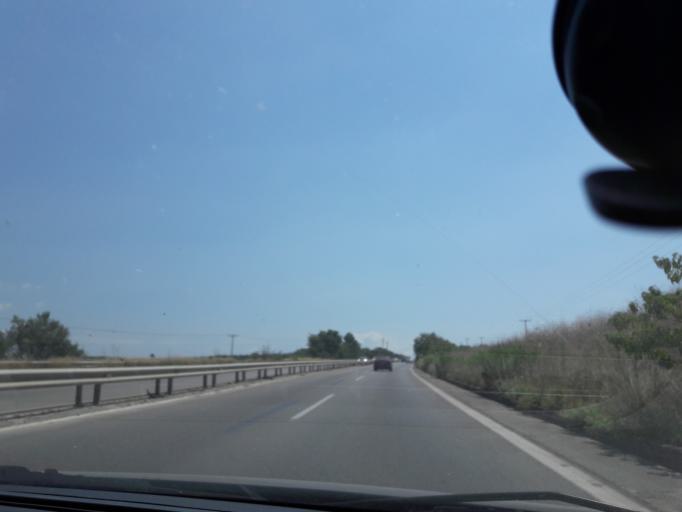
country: GR
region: Central Macedonia
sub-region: Nomos Chalkidikis
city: Nea Kallikrateia
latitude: 40.3042
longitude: 23.1313
